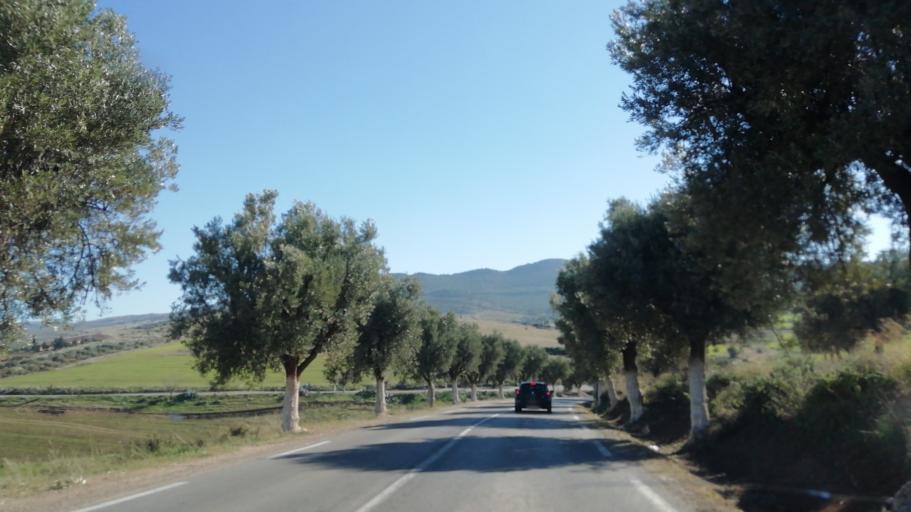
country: DZ
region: Tlemcen
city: Beni Mester
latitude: 34.8330
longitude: -1.5021
